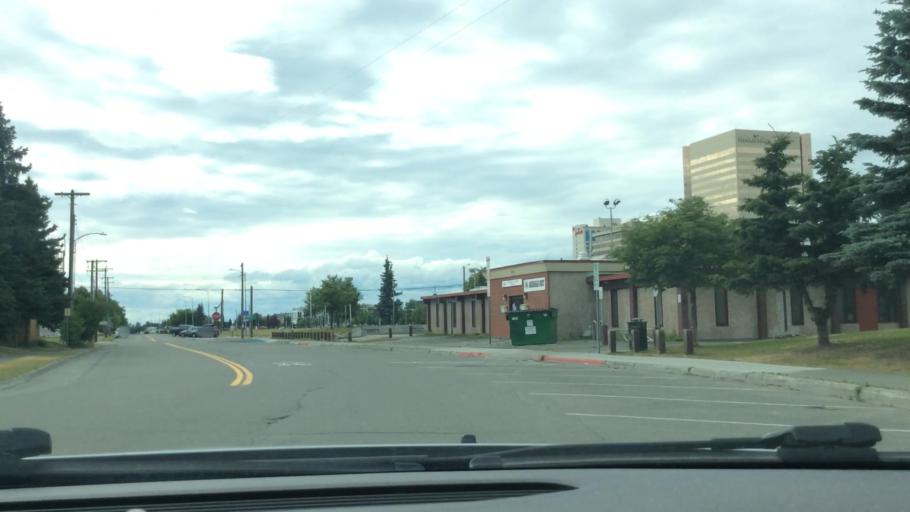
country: US
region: Alaska
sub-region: Anchorage Municipality
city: Anchorage
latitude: 61.2127
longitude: -149.8891
